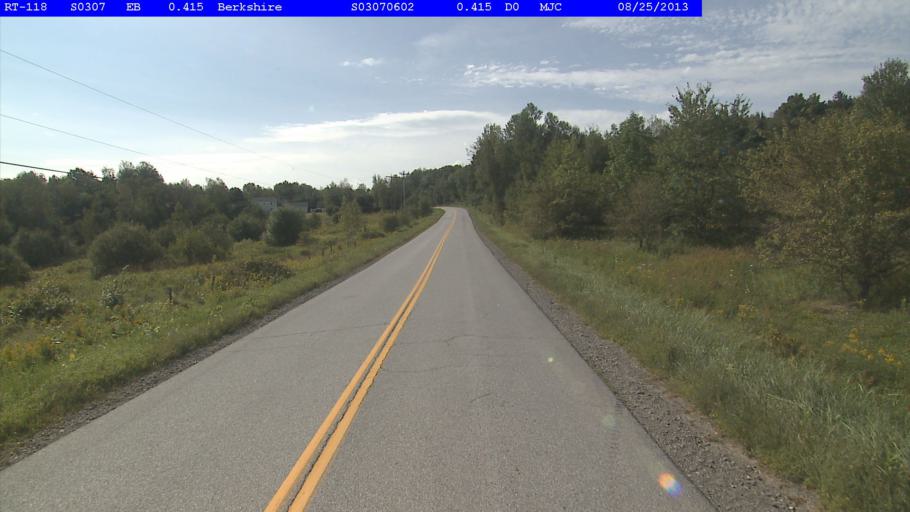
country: US
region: Vermont
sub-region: Franklin County
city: Richford
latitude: 44.9349
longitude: -72.7197
